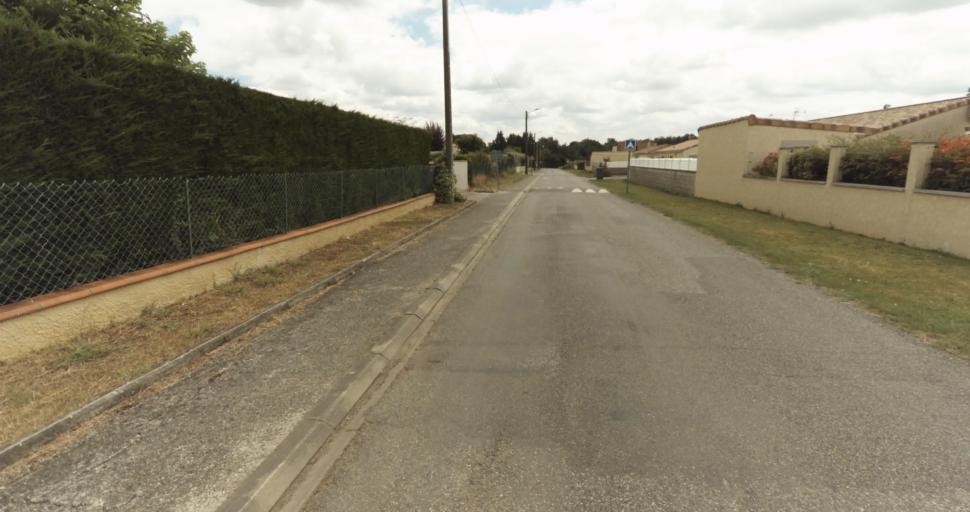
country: FR
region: Midi-Pyrenees
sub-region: Departement de la Haute-Garonne
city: Fontenilles
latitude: 43.5562
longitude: 1.1838
